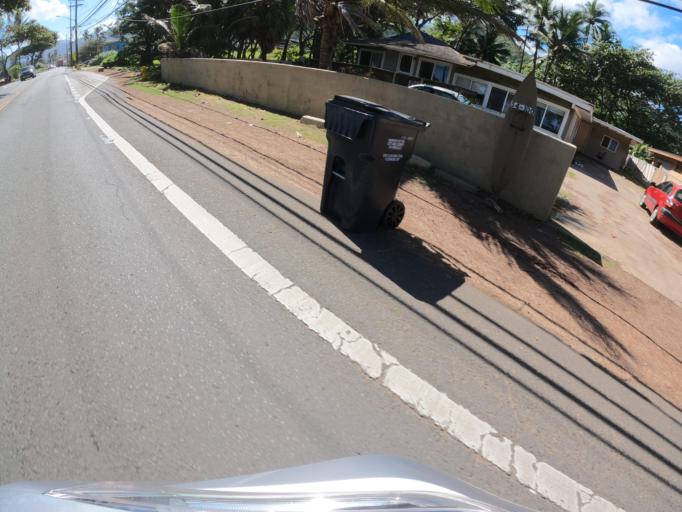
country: US
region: Hawaii
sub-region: Honolulu County
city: Hau'ula
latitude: 21.6096
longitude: -157.9097
